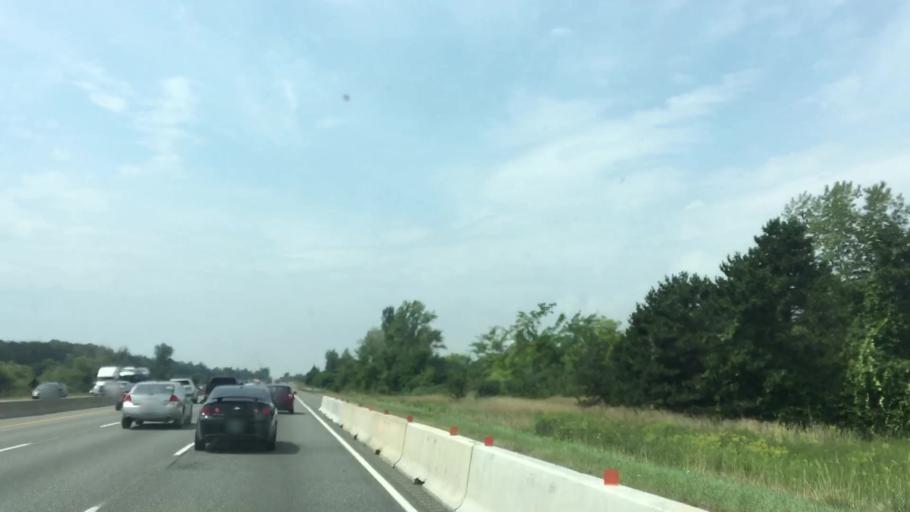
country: CA
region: Ontario
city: Oshawa
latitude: 43.8777
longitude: -78.7797
